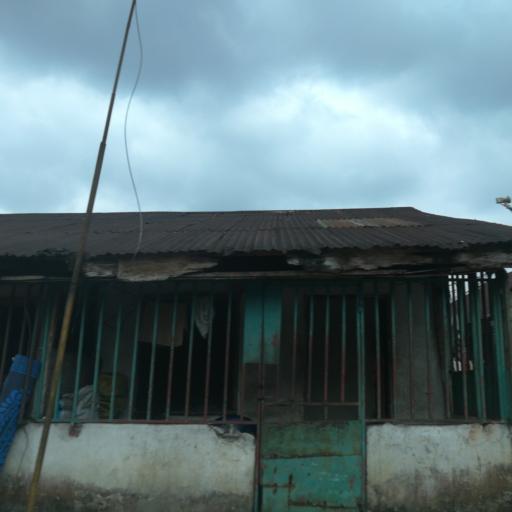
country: NG
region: Rivers
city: Port Harcourt
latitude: 4.8260
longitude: 7.0415
